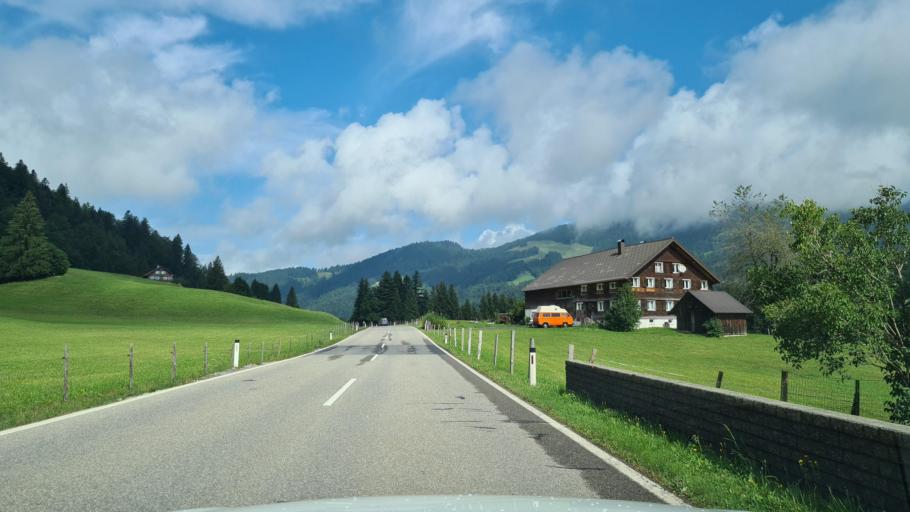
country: AT
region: Vorarlberg
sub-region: Politischer Bezirk Bregenz
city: Sibratsgfall
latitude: 47.4503
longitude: 10.0038
